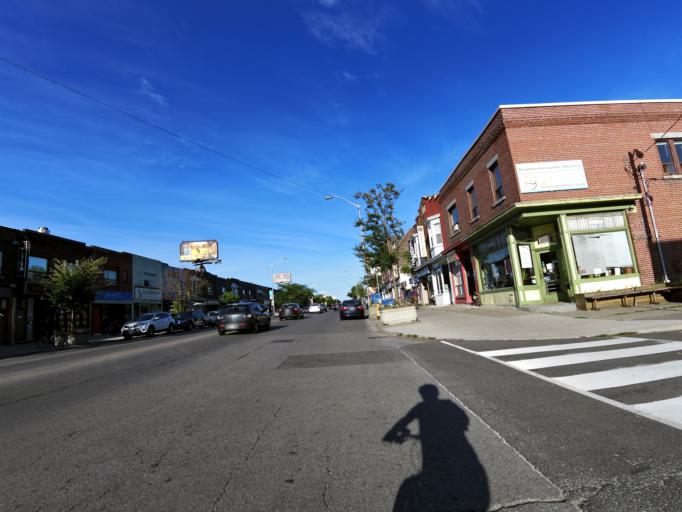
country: CA
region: Ontario
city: Toronto
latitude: 43.6820
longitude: -79.3294
